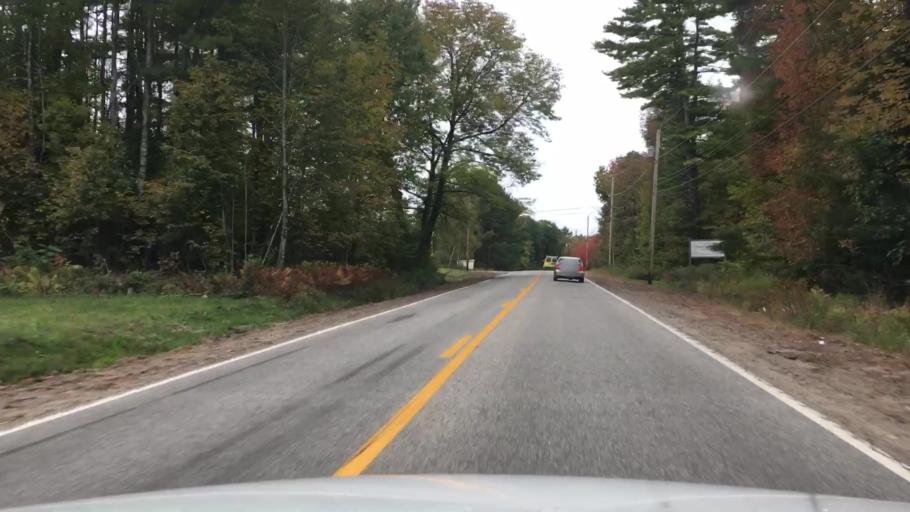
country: US
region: Maine
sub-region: Oxford County
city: Norway
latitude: 44.2206
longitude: -70.5948
